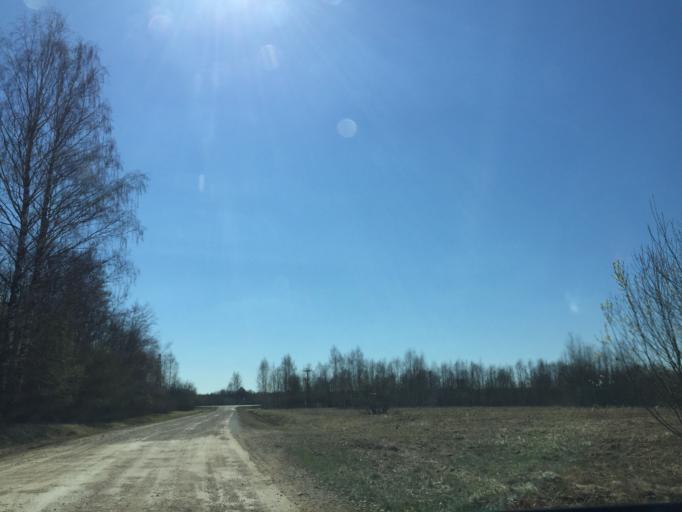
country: EE
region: Viljandimaa
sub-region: Viiratsi vald
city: Viiratsi
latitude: 58.3987
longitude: 25.8716
